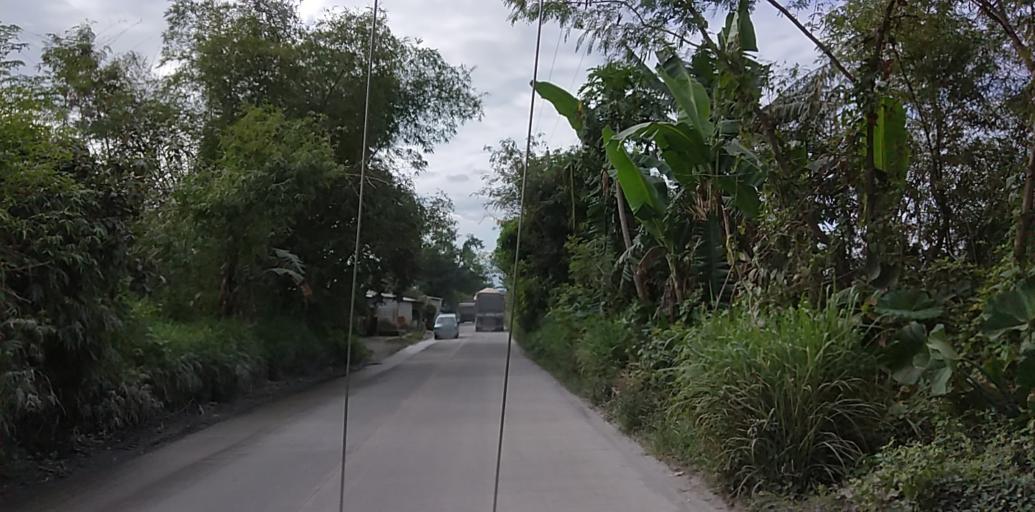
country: PH
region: Central Luzon
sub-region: Province of Pampanga
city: Porac
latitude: 15.0687
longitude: 120.5560
